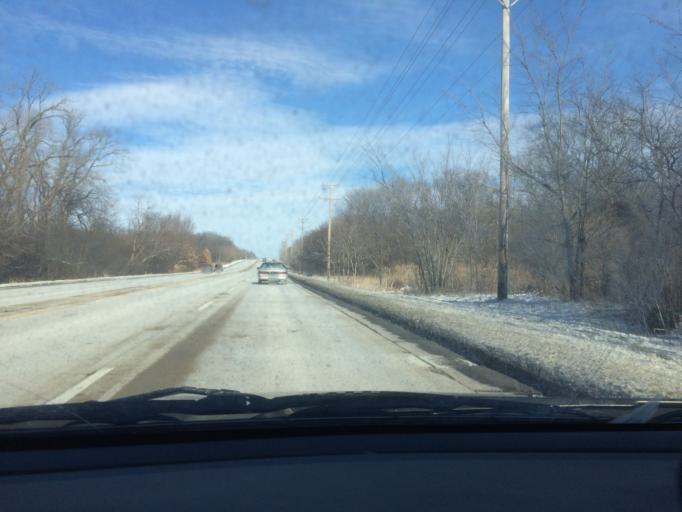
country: US
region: Illinois
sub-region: Cook County
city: Streamwood
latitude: 42.0546
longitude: -88.1934
